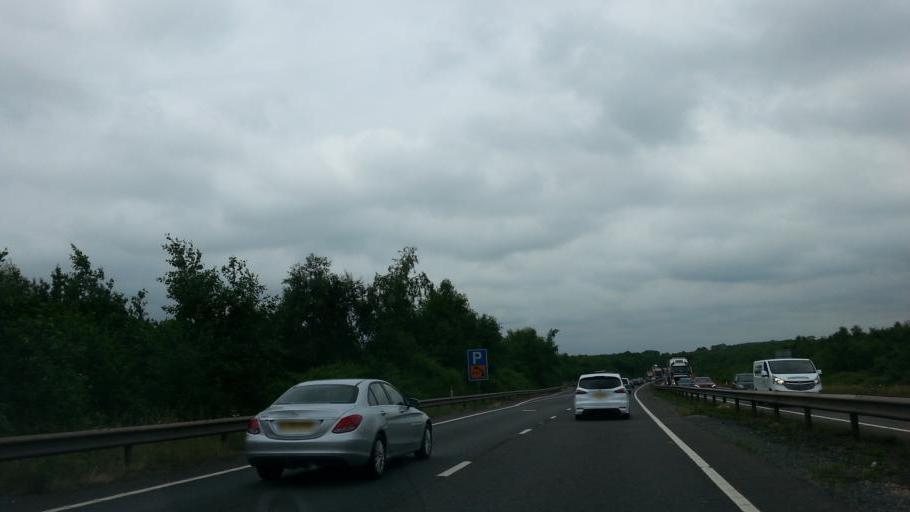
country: GB
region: England
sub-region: Leicestershire
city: Ashby de la Zouch
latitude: 52.7642
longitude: -1.4315
